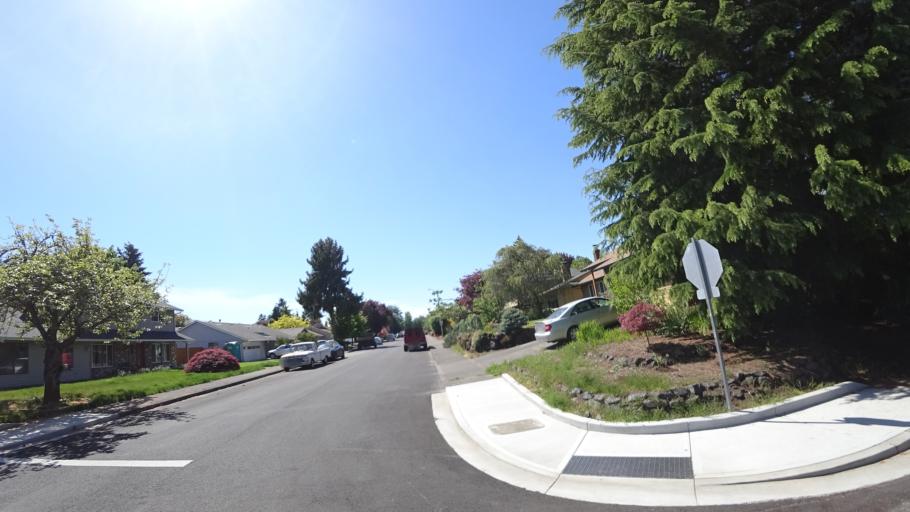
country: US
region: Oregon
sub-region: Washington County
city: Hillsboro
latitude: 45.5101
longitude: -122.9537
